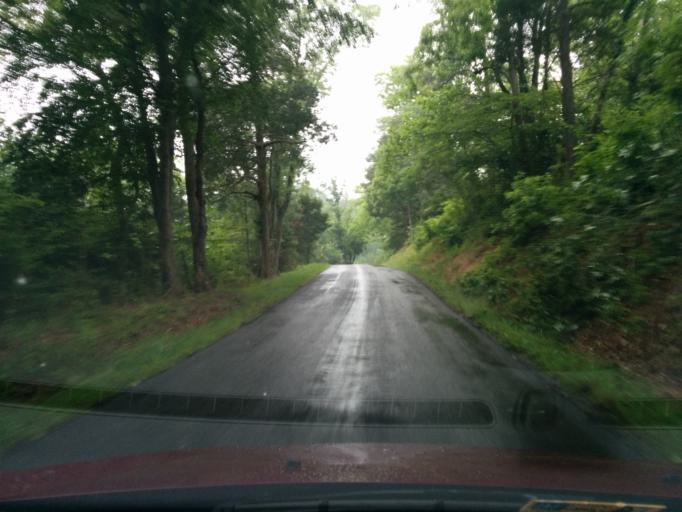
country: US
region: Virginia
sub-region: Rockbridge County
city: East Lexington
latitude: 37.8554
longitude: -79.4235
